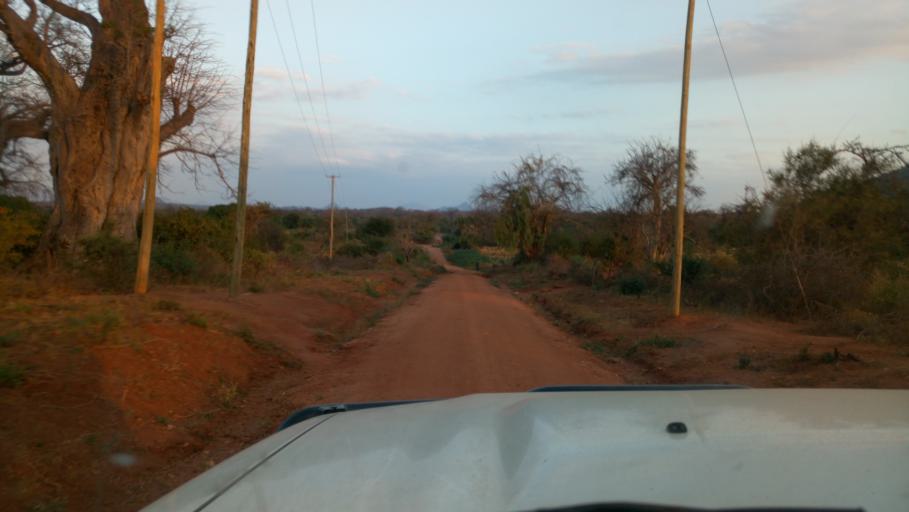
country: KE
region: Kitui
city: Kitui
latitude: -1.6806
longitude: 38.2232
